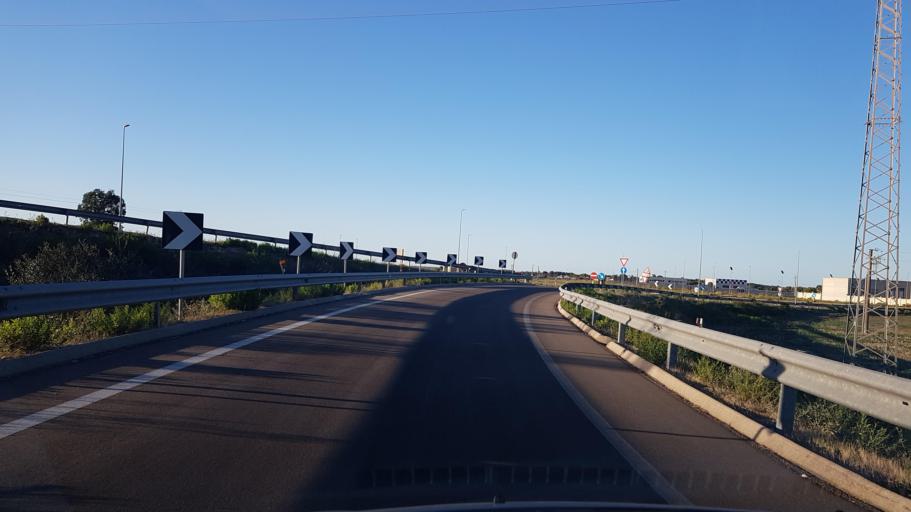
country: IT
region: Apulia
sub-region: Provincia di Brindisi
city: San Pancrazio Salentino
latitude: 40.4145
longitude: 17.8103
